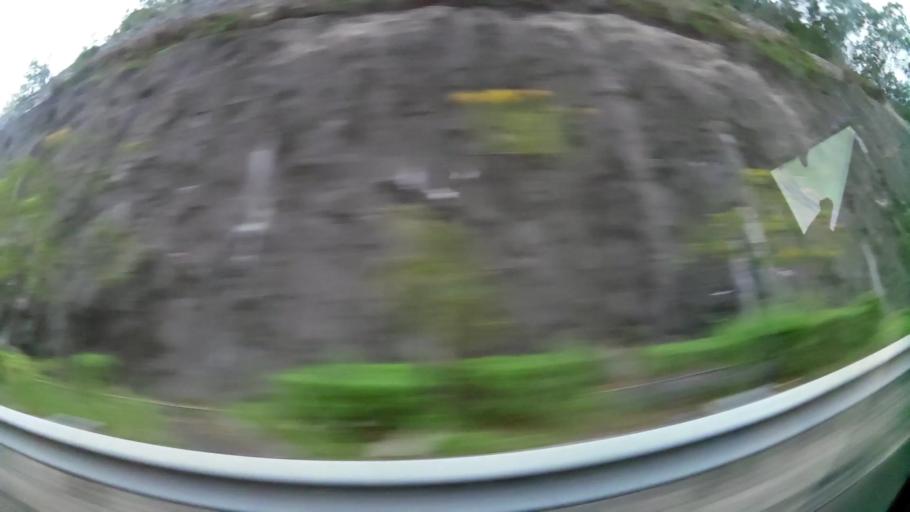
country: HK
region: Tsuen Wan
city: Tsuen Wan
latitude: 22.3580
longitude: 114.0833
